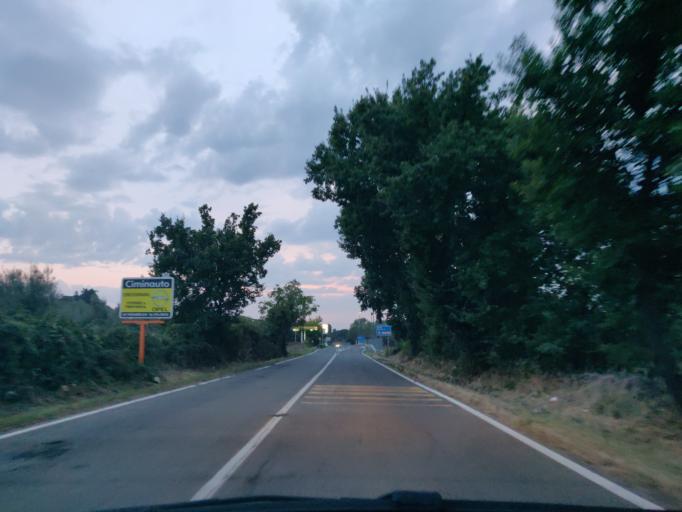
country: IT
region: Latium
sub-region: Provincia di Viterbo
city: Vetralla
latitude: 42.3739
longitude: 12.0636
